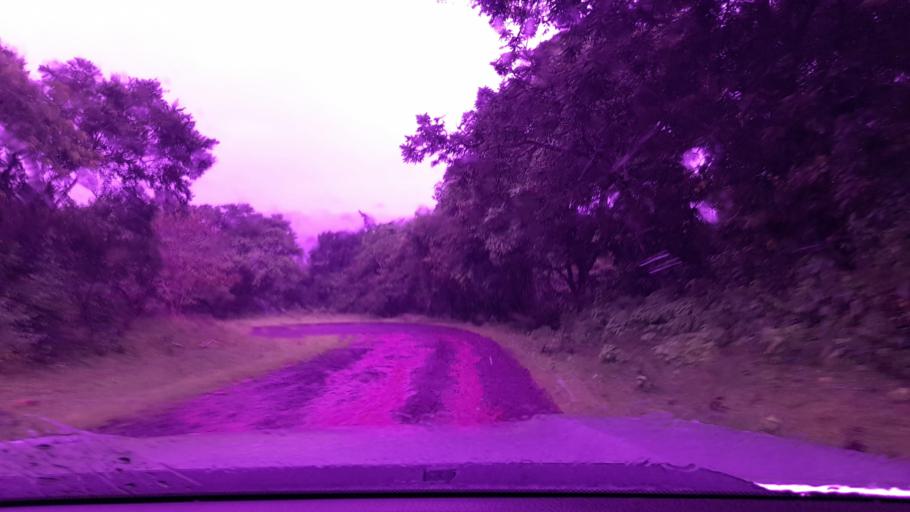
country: ET
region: Oromiya
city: Metu
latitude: 8.4755
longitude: 35.6410
